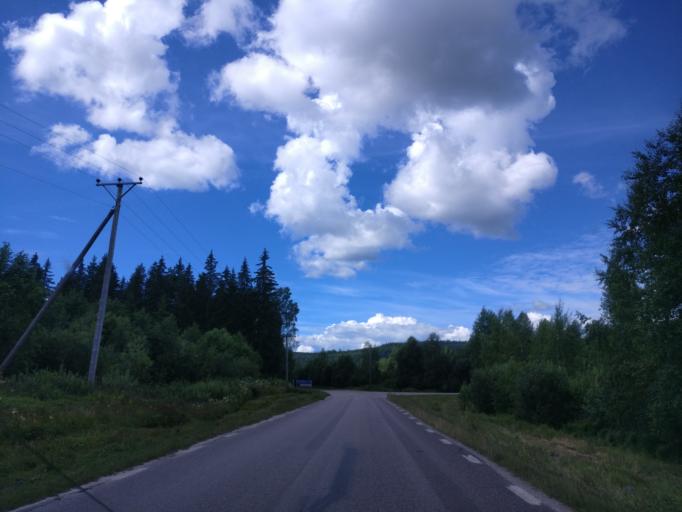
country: SE
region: Vaermland
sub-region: Hagfors Kommun
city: Ekshaerad
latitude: 60.0390
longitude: 13.4993
